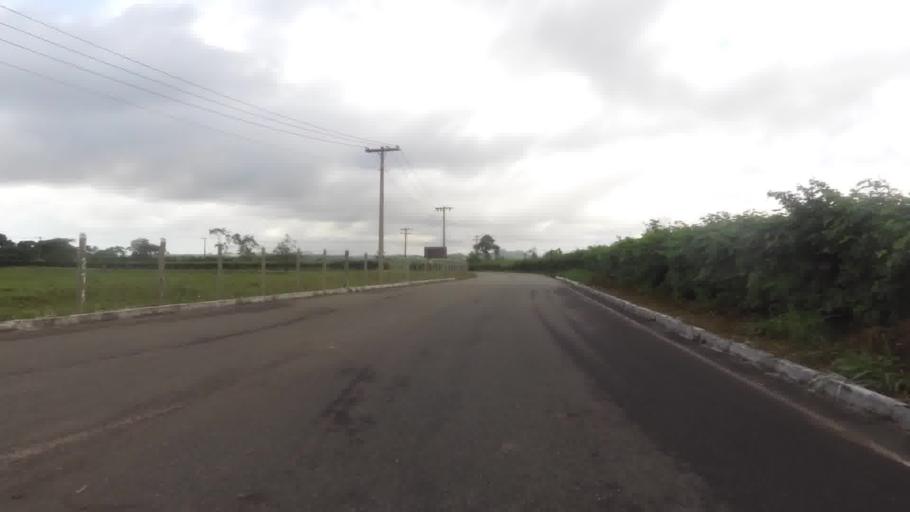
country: BR
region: Espirito Santo
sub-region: Piuma
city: Piuma
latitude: -20.7648
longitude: -40.6298
